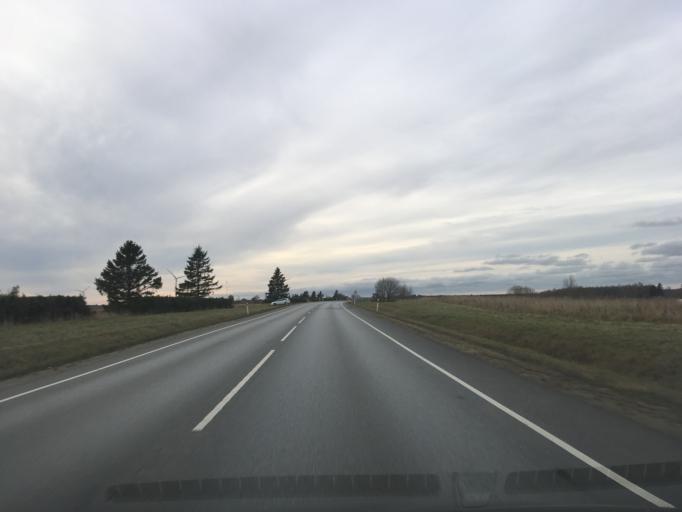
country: EE
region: Ida-Virumaa
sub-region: Aseri vald
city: Aseri
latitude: 59.4405
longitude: 26.8037
